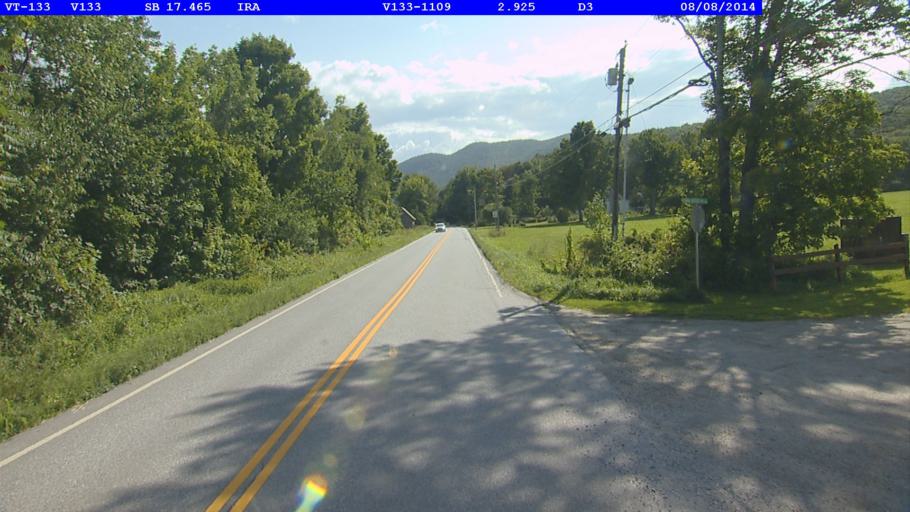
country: US
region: Vermont
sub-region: Rutland County
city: West Rutland
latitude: 43.5340
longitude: -73.0629
